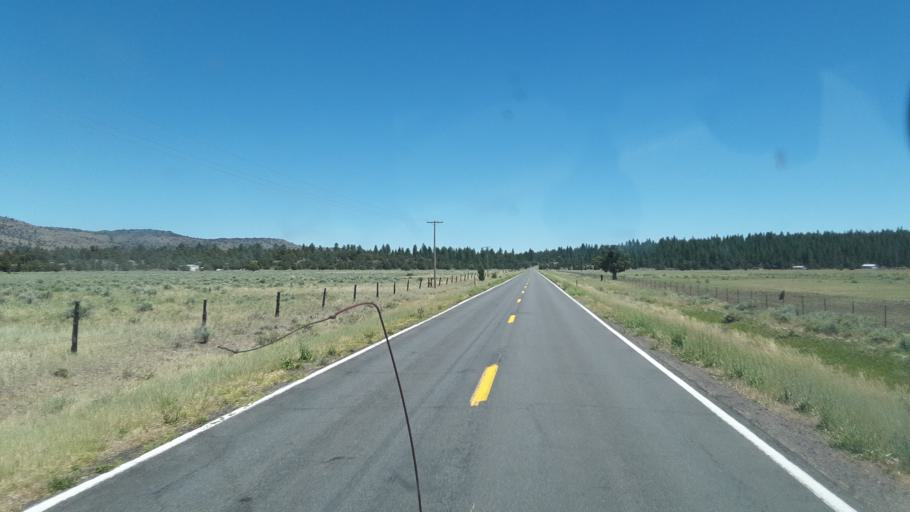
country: US
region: California
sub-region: Lassen County
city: Susanville
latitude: 40.5217
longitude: -120.5888
